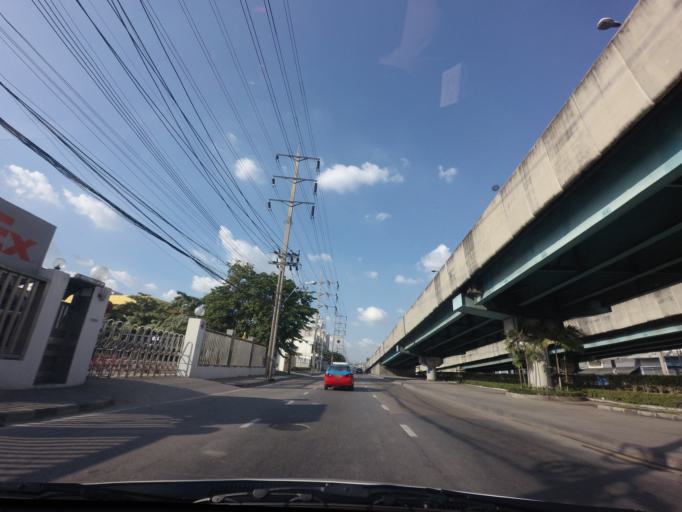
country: TH
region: Bangkok
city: Yan Nawa
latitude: 13.6870
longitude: 100.5476
